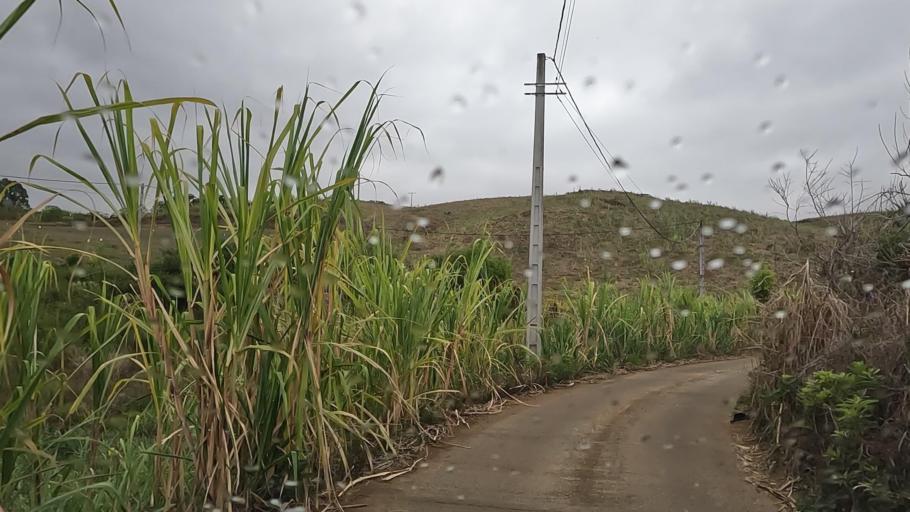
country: RE
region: Reunion
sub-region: Reunion
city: Le Tampon
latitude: -21.2899
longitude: 55.5446
